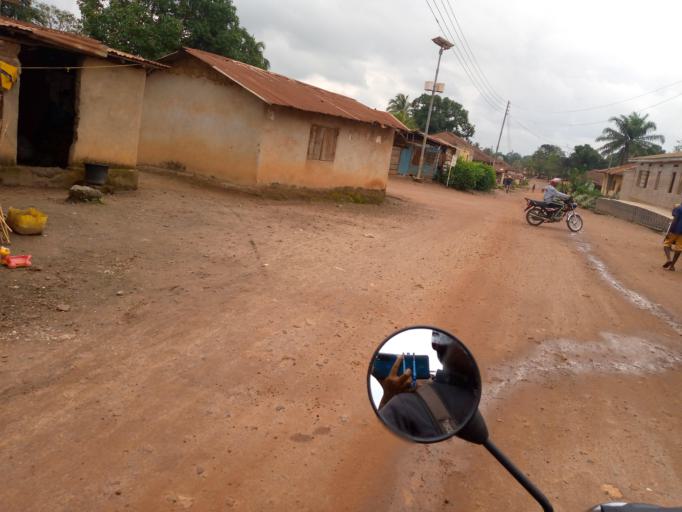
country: SL
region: Eastern Province
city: Kenema
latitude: 7.8638
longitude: -11.1951
